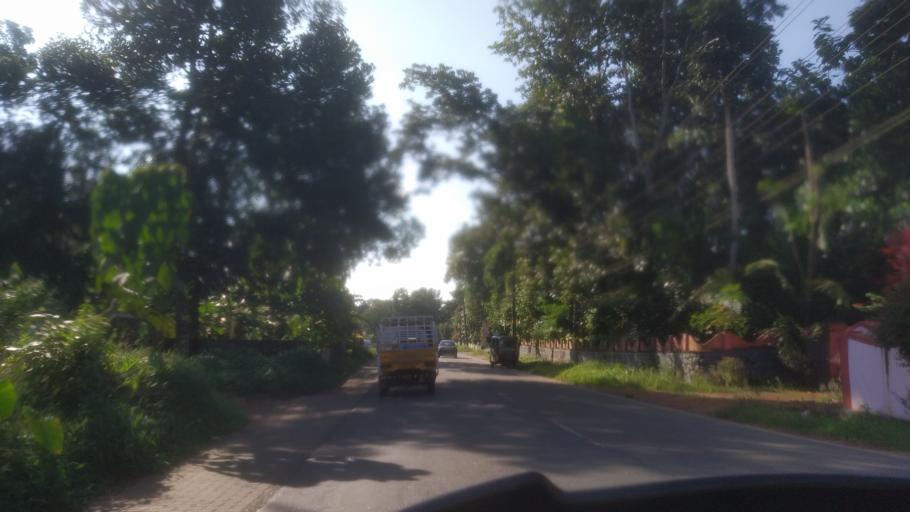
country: IN
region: Kerala
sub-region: Ernakulam
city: Muvattupuzha
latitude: 9.9786
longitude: 76.5251
